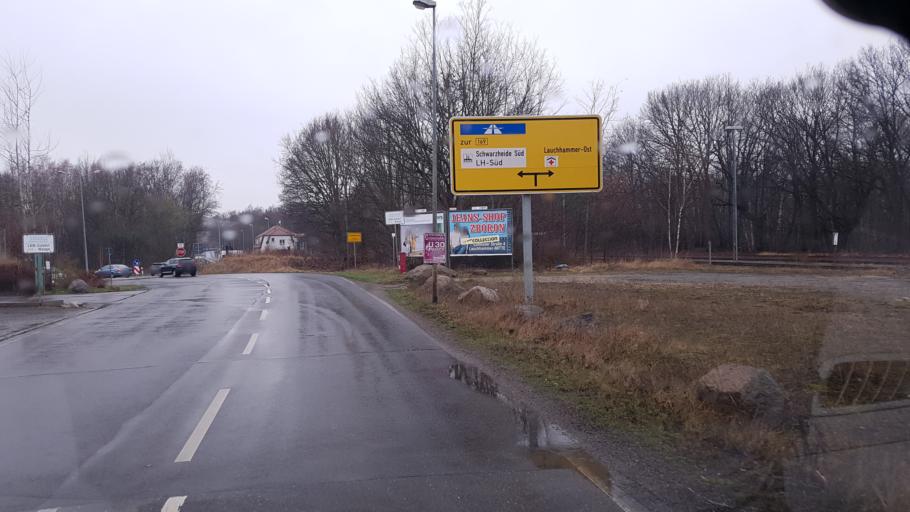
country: DE
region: Brandenburg
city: Lauchhammer
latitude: 51.4971
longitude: 13.8085
